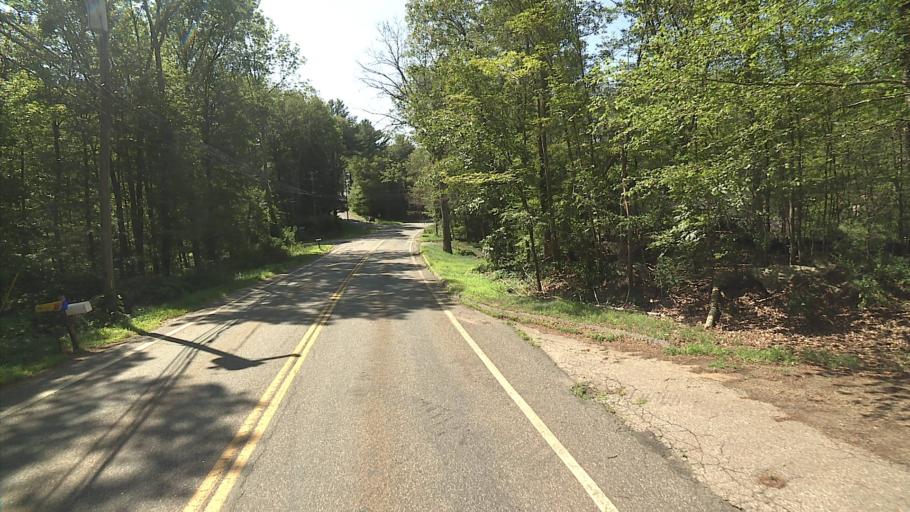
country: US
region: Connecticut
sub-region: Tolland County
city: Storrs
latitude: 41.9031
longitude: -72.1691
